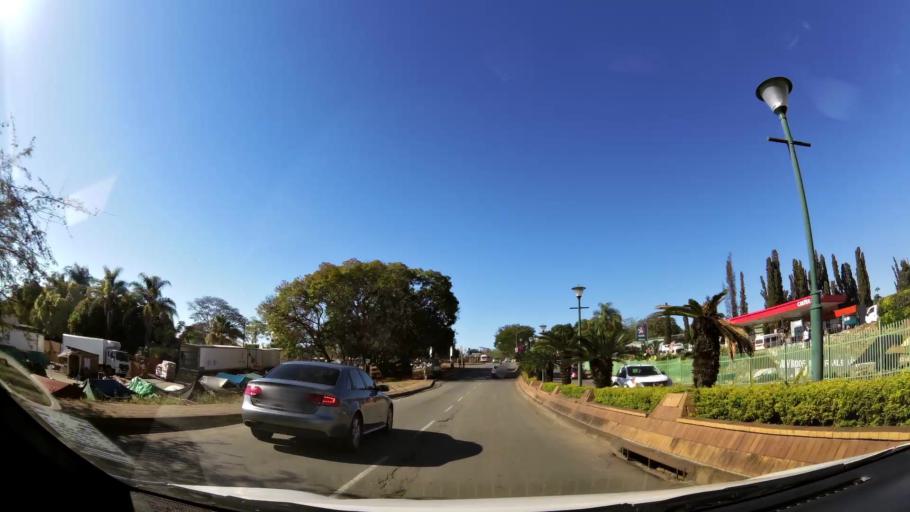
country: ZA
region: Limpopo
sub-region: Mopani District Municipality
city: Tzaneen
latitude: -23.8295
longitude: 30.1628
